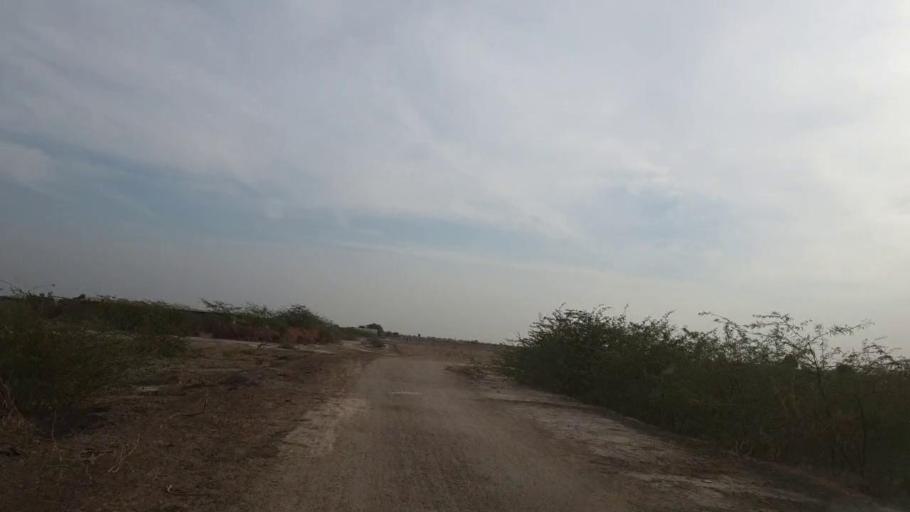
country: PK
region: Sindh
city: Nabisar
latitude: 24.9940
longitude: 69.5182
